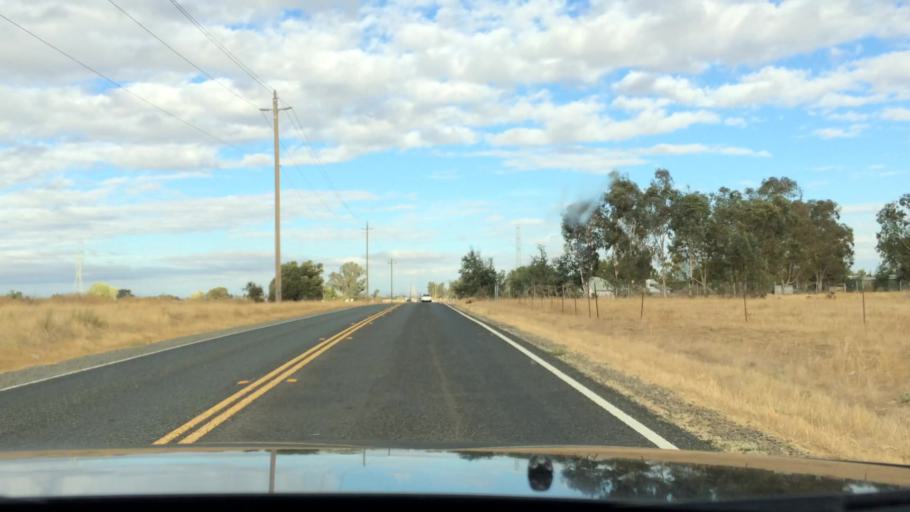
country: US
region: California
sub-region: Sacramento County
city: Herald
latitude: 38.3038
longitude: -121.2294
